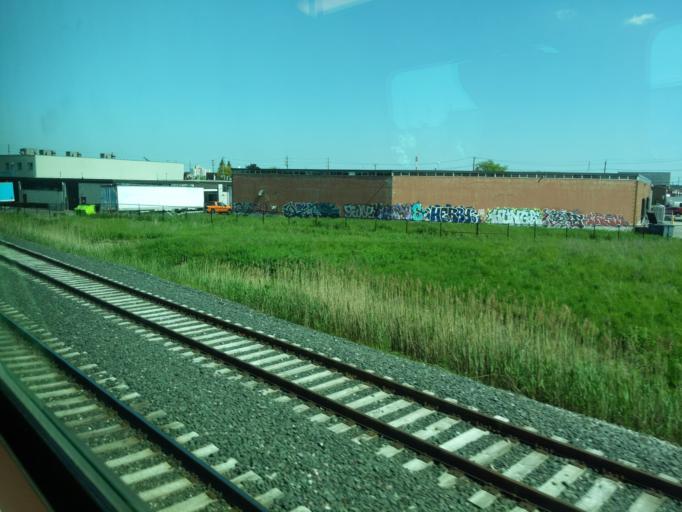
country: CA
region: Ontario
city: Etobicoke
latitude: 43.7060
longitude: -79.5800
